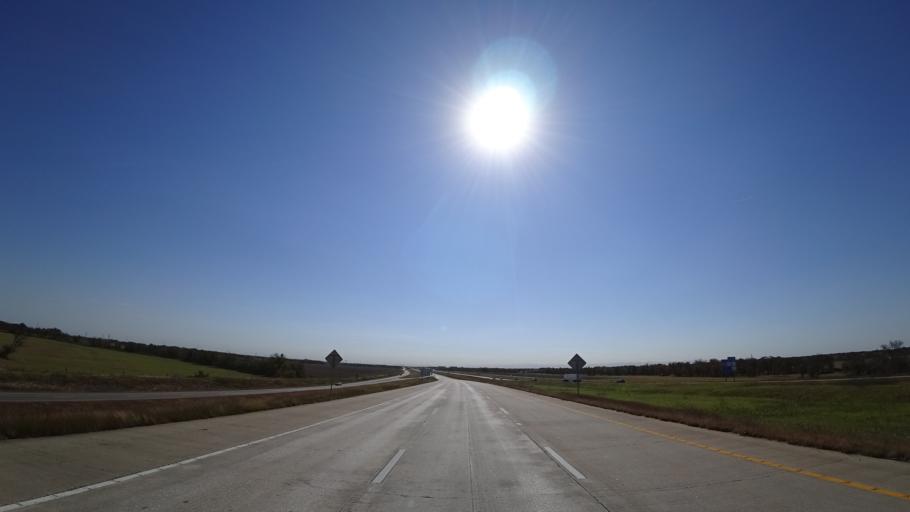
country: US
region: Texas
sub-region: Travis County
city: Pflugerville
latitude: 30.4489
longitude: -97.5938
